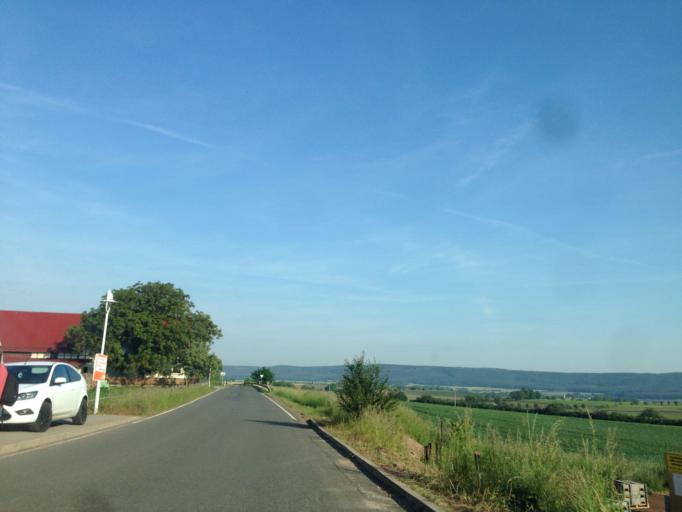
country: DE
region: Thuringia
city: Seisla
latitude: 50.6538
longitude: 11.5193
